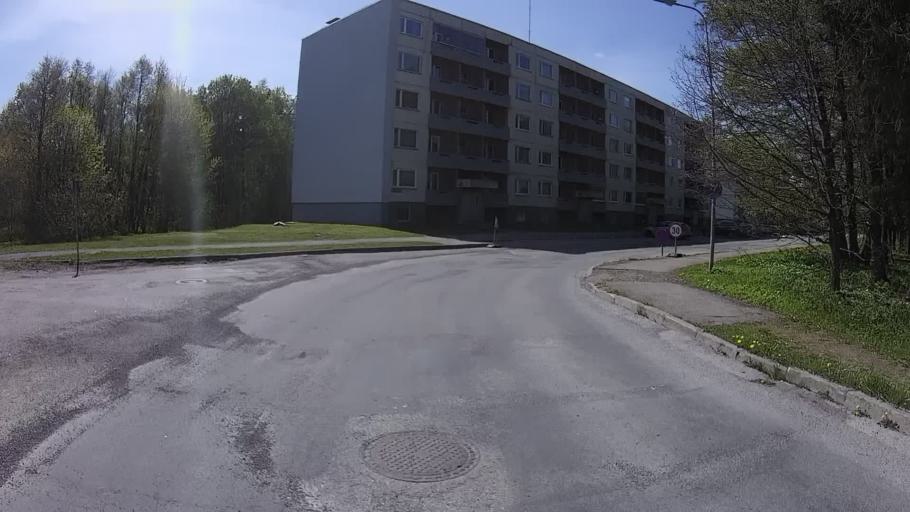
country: EE
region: Laeaene
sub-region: Haapsalu linn
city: Haapsalu
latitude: 58.9349
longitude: 23.5612
